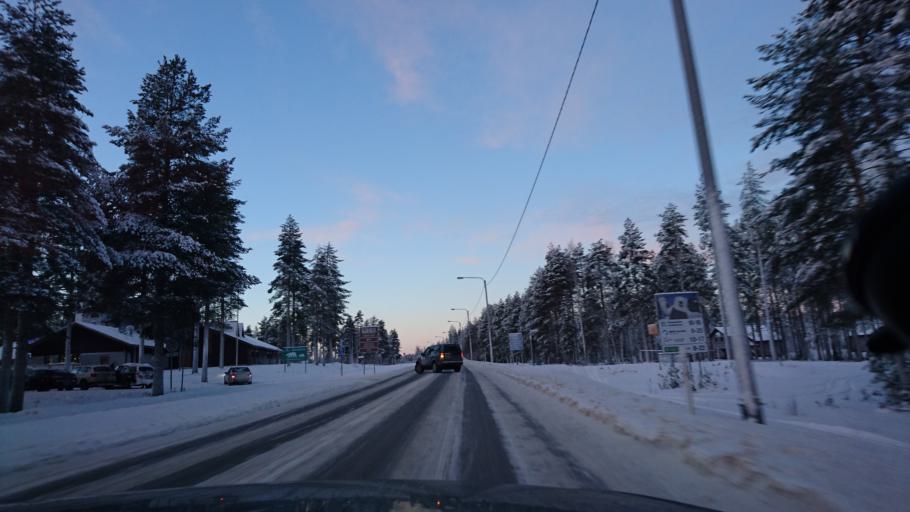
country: FI
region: Lapland
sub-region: Rovaniemi
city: Ranua
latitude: 65.9438
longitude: 26.4693
